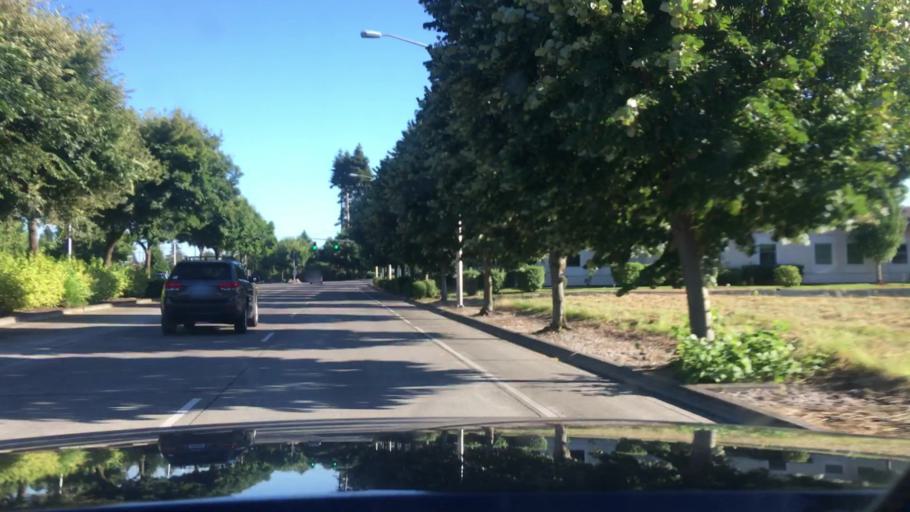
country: US
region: Oregon
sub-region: Lane County
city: Springfield
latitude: 44.0790
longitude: -123.0311
